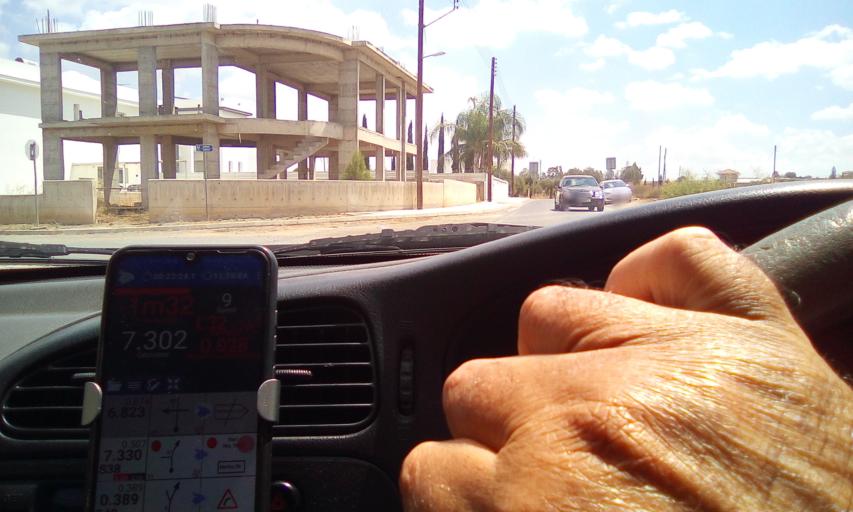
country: CY
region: Lefkosia
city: Psimolofou
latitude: 35.0564
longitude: 33.2681
